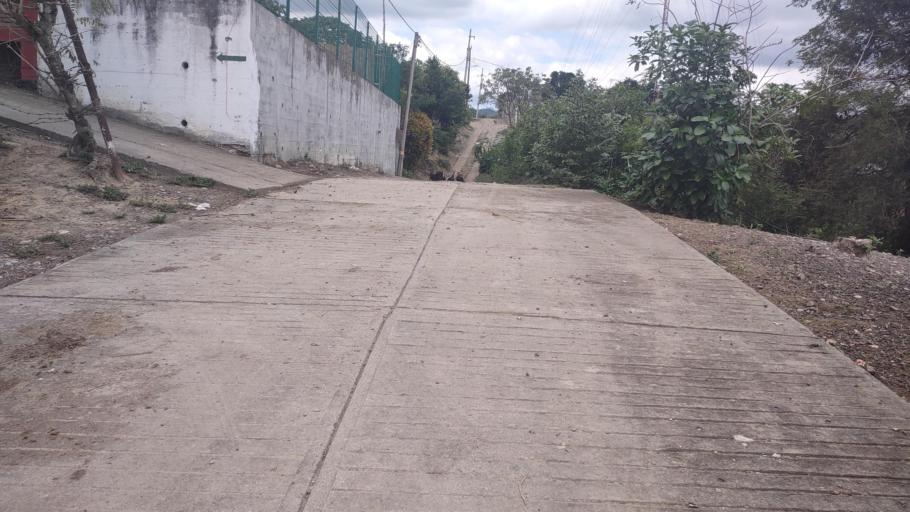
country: MX
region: Veracruz
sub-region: Papantla
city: Polutla
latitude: 20.4644
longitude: -97.2571
